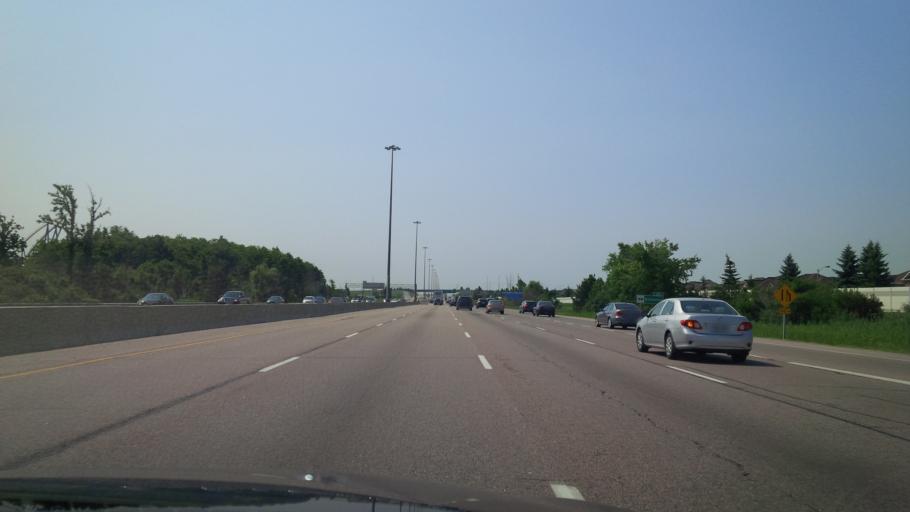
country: CA
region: Ontario
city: Vaughan
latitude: 43.8412
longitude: -79.5477
